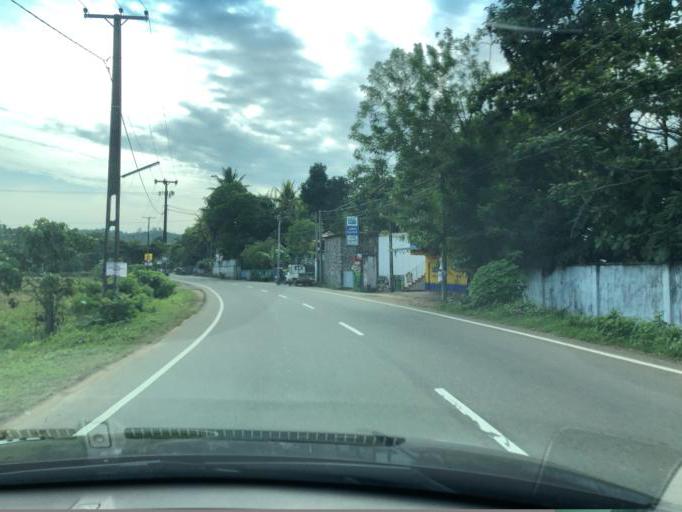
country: LK
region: Western
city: Kalutara
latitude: 6.5656
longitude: 79.9945
